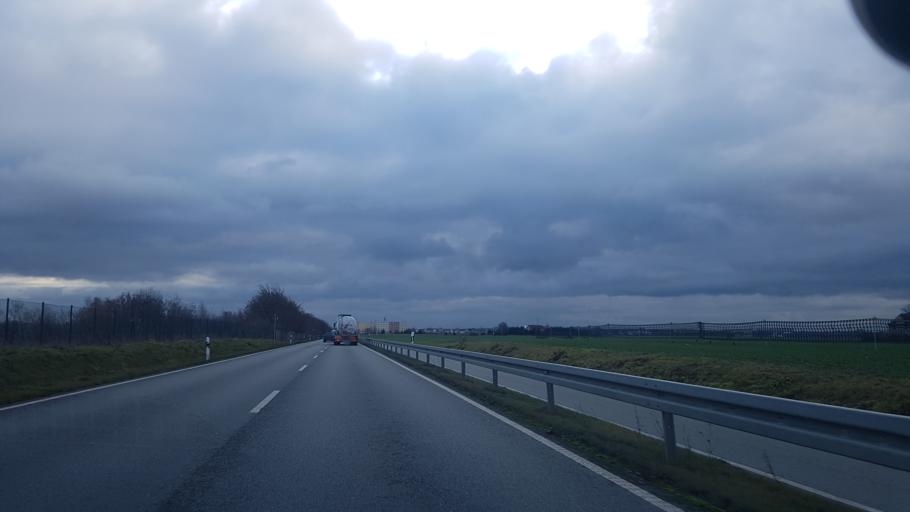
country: DE
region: Saxony
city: Grossenhain
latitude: 51.3132
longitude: 13.5387
